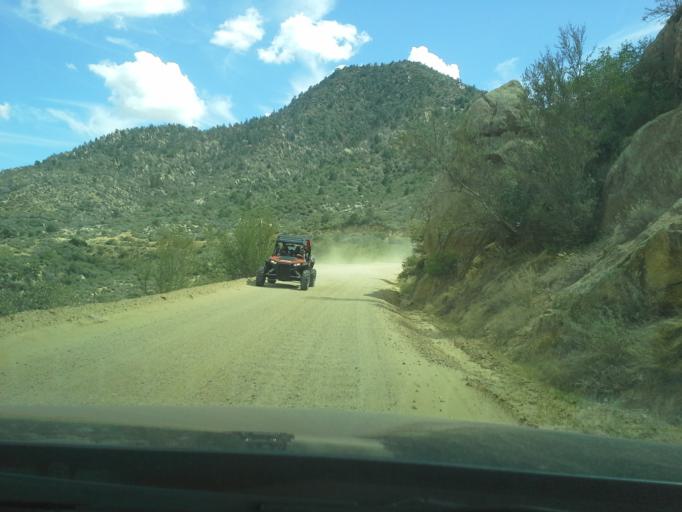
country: US
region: Arizona
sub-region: Yavapai County
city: Mayer
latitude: 34.2495
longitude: -112.2967
